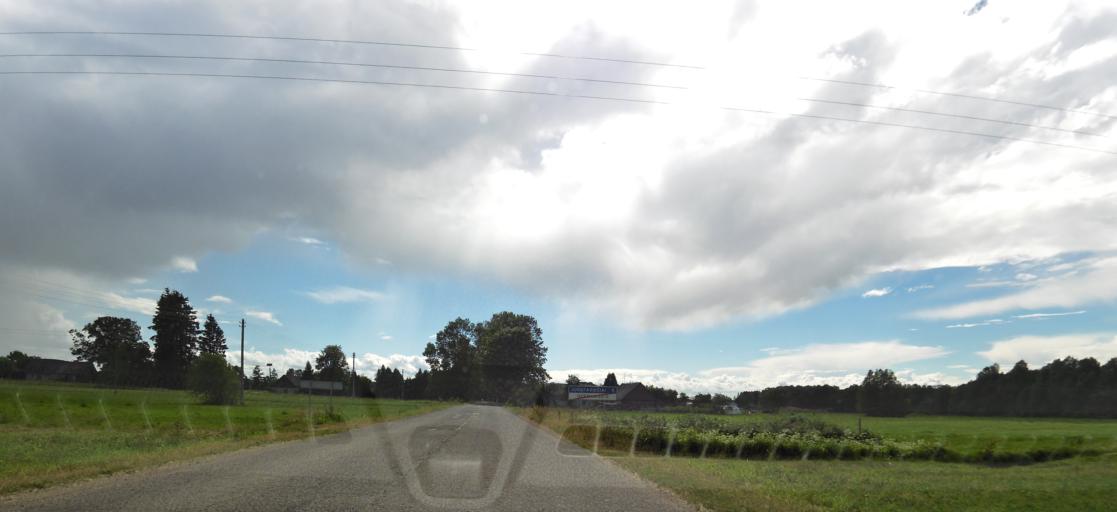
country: LT
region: Panevezys
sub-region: Birzai
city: Birzai
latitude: 56.3715
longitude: 24.6407
